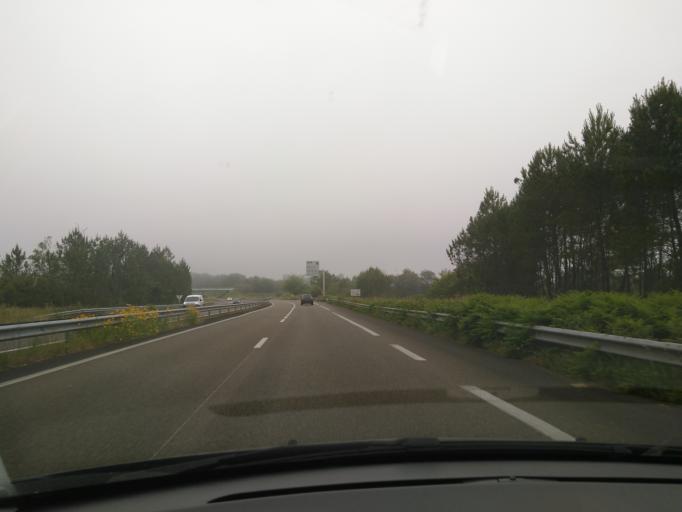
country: FR
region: Aquitaine
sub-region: Departement des Landes
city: Meilhan
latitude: 43.8642
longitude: -0.6860
